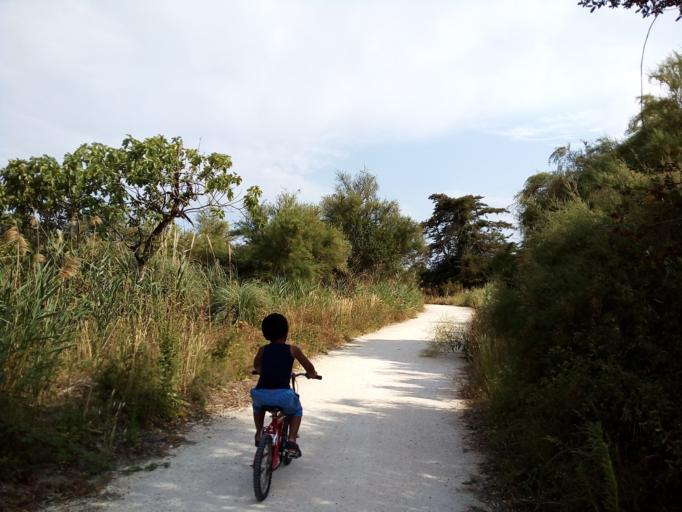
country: FR
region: Poitou-Charentes
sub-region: Departement de la Charente-Maritime
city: Boyard-Ville
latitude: 45.9547
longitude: -1.2448
